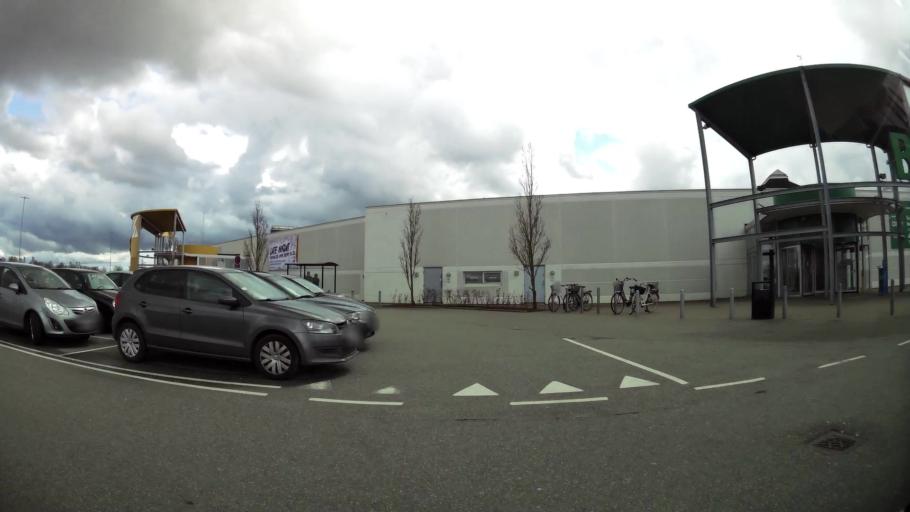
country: DK
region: South Denmark
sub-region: Kolding Kommune
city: Kolding
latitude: 55.5148
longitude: 9.4588
